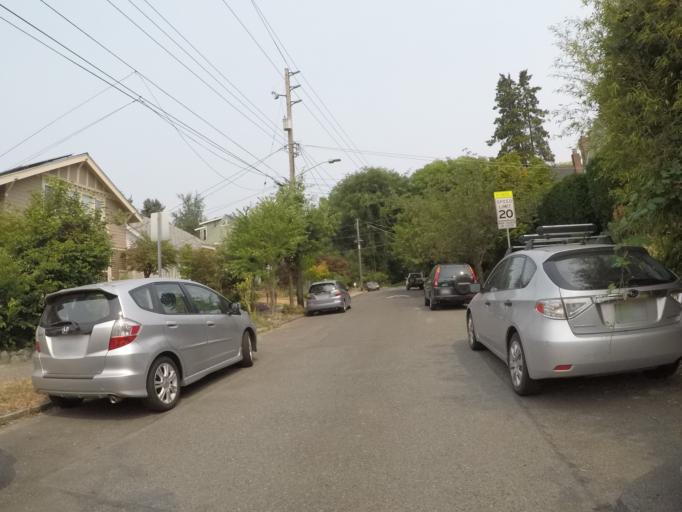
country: US
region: Washington
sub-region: King County
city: Seattle
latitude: 47.6245
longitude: -122.3047
